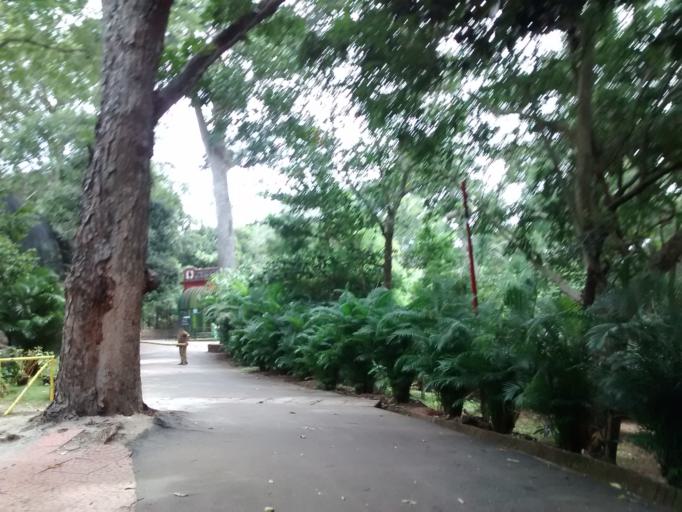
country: IN
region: Kerala
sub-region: Thiruvananthapuram
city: Thiruvananthapuram
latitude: 8.5099
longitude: 76.9542
